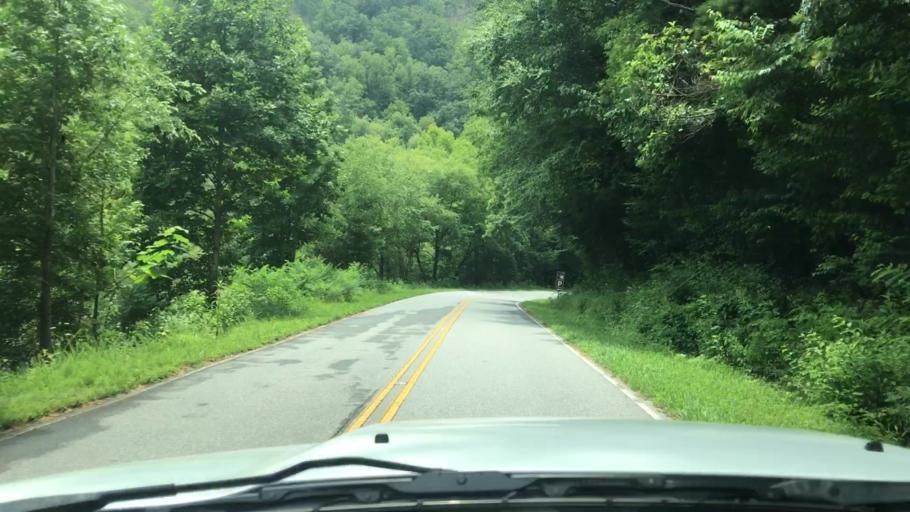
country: US
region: North Carolina
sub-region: Graham County
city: Robbinsville
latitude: 35.4238
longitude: -83.8999
